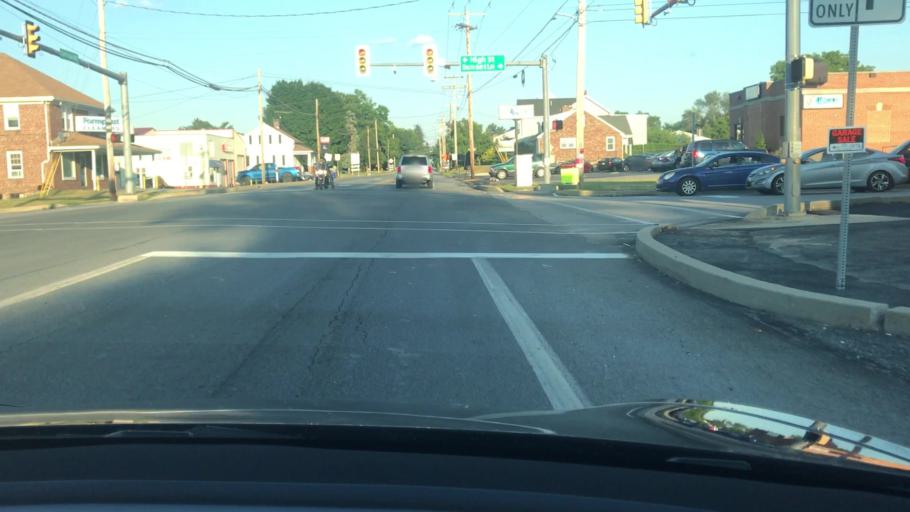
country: US
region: Pennsylvania
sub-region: York County
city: Shiloh
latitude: 39.9763
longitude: -76.7923
